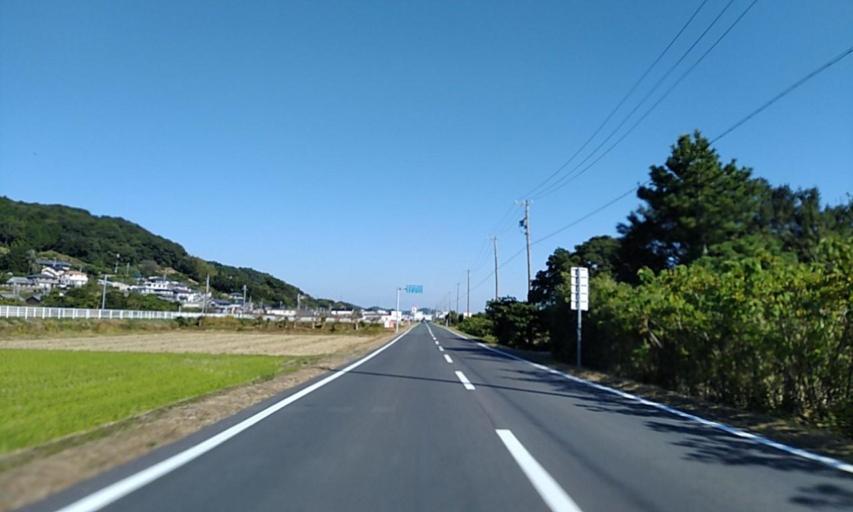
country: JP
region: Shizuoka
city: Kosai-shi
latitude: 34.8061
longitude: 137.6376
